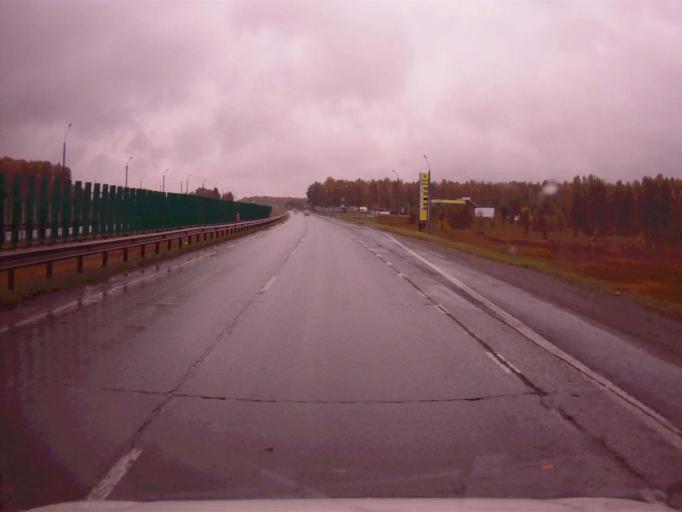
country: RU
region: Chelyabinsk
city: Dolgoderevenskoye
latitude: 55.3244
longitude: 61.3307
